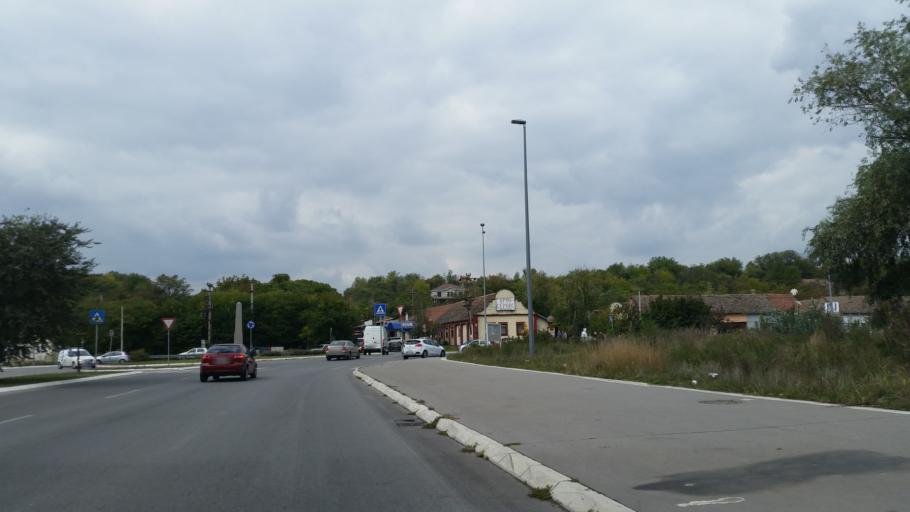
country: RS
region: Central Serbia
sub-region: Belgrade
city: Zemun
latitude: 44.8032
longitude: 20.3669
